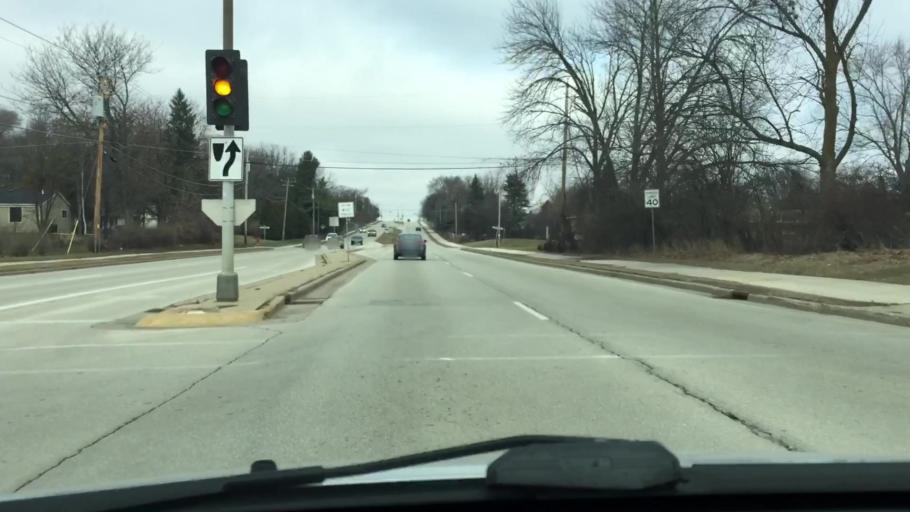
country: US
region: Wisconsin
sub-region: Waukesha County
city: Waukesha
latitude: 43.0249
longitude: -88.1667
